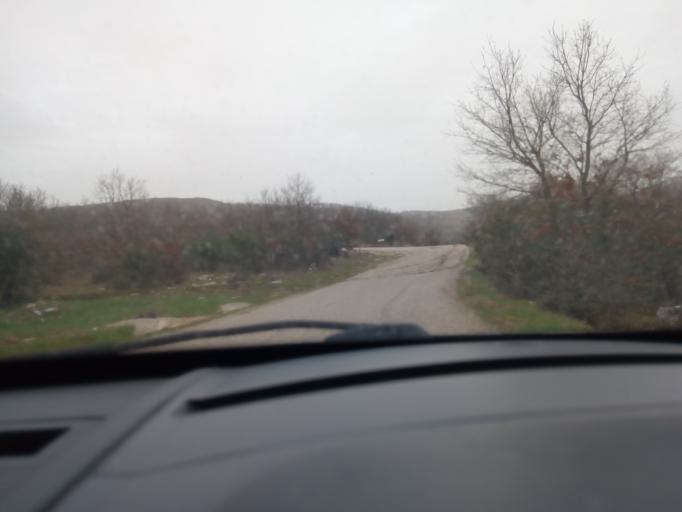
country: TR
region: Balikesir
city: Omerkoy
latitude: 39.9221
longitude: 28.0618
